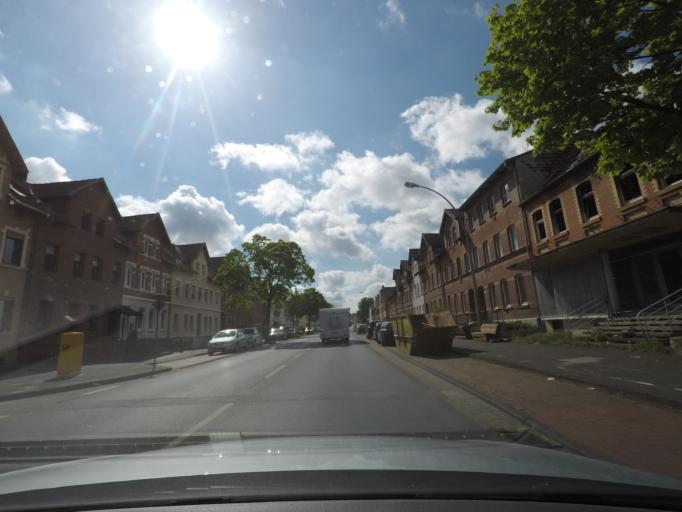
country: DE
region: Lower Saxony
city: Helmstedt
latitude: 52.2353
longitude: 11.0037
